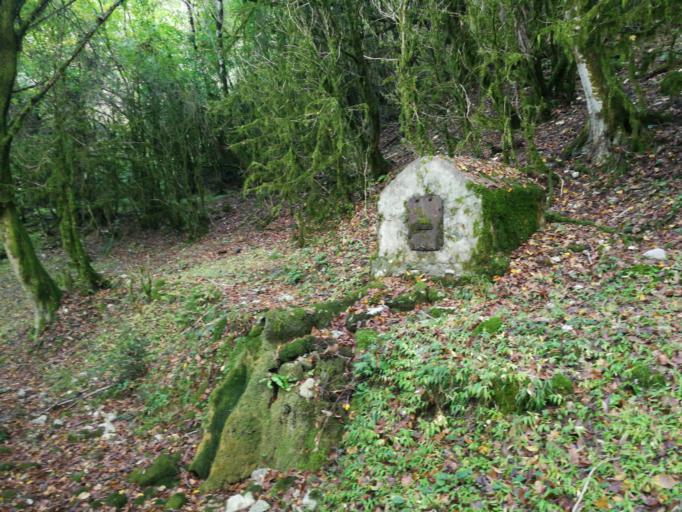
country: GE
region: Abkhazia
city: Gagra
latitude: 43.3282
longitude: 40.2614
